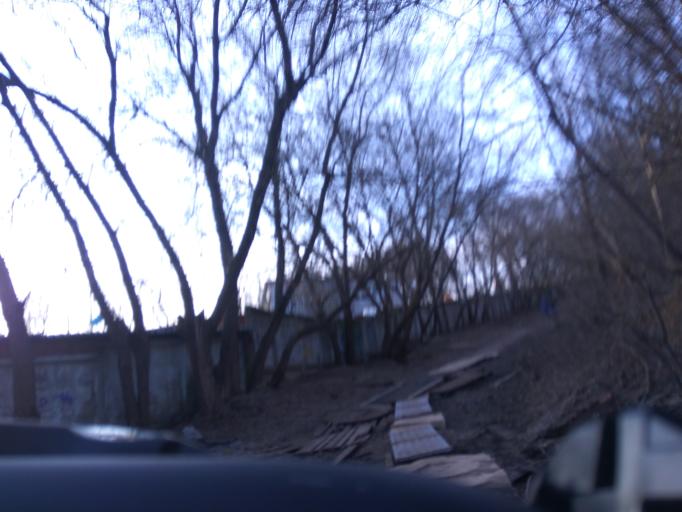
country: RU
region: Moscow
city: Vorob'yovo
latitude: 55.7280
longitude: 37.5174
